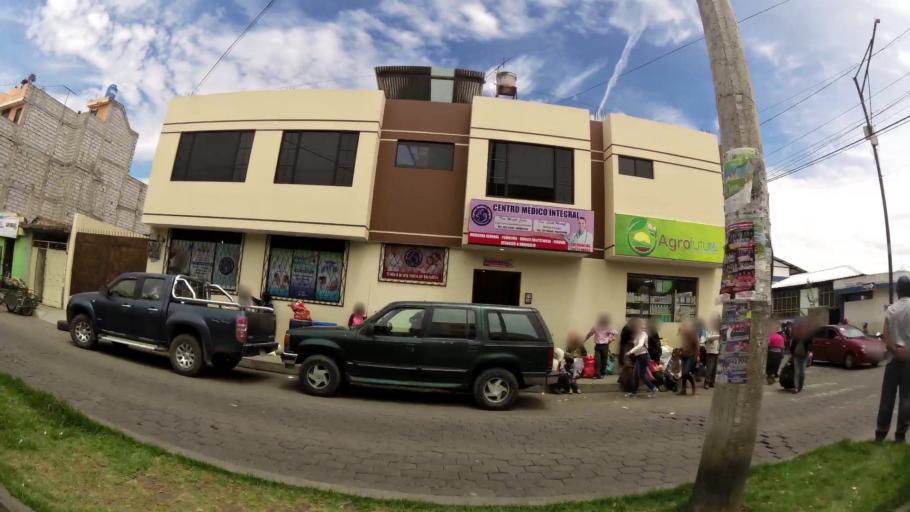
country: EC
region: Cotopaxi
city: San Miguel de Salcedo
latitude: -1.0458
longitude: -78.5886
